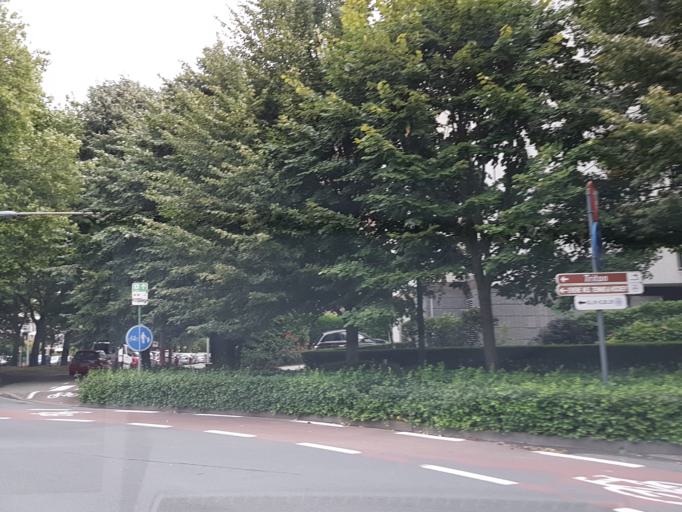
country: BE
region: Flanders
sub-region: Provincie Vlaams-Brabant
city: Diegem
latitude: 50.8626
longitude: 4.4113
